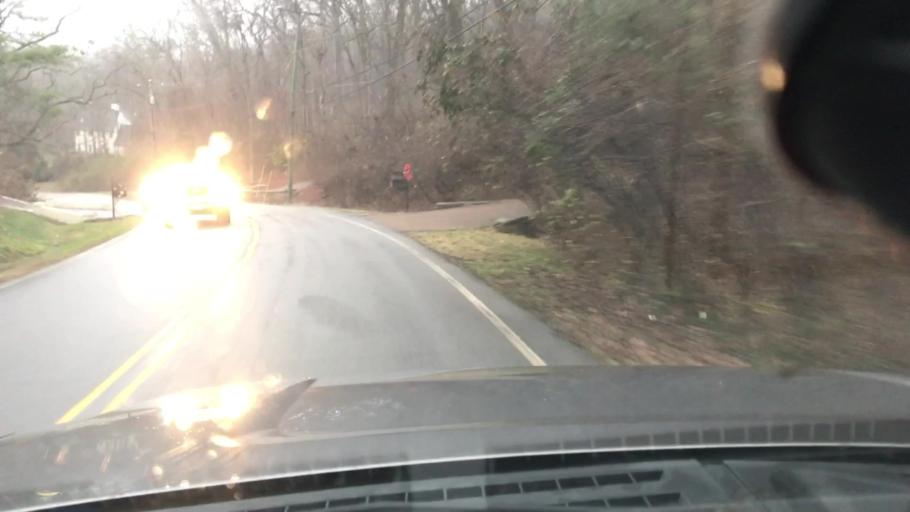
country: US
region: Tennessee
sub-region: Davidson County
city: Forest Hills
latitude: 36.0682
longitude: -86.8587
